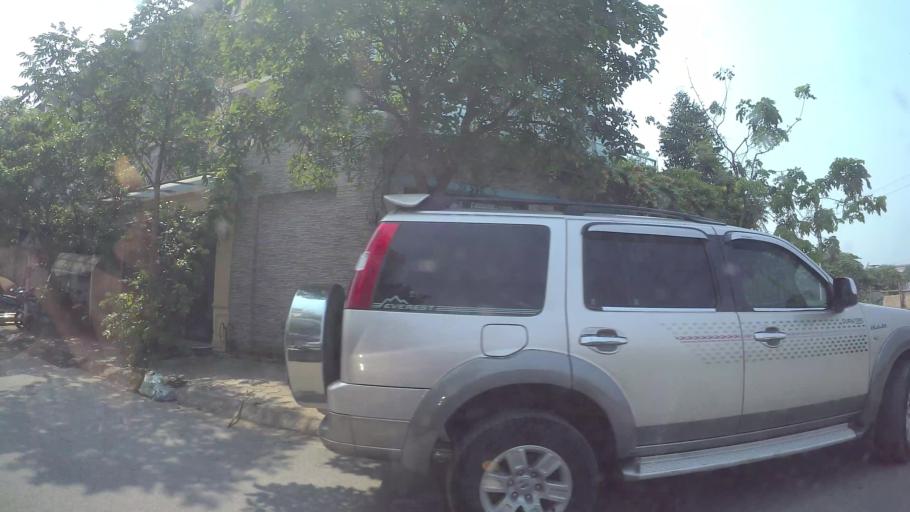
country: VN
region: Ha Noi
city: Ha Dong
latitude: 20.9703
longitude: 105.8001
